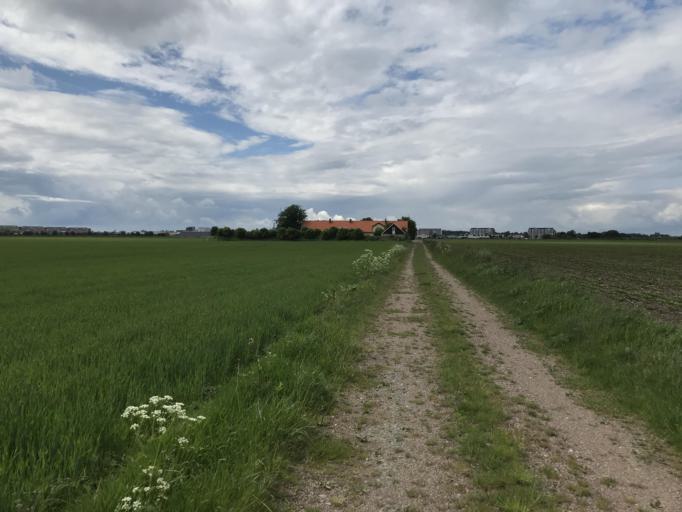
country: SE
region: Skane
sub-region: Landskrona
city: Landskrona
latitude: 55.8861
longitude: 12.8688
